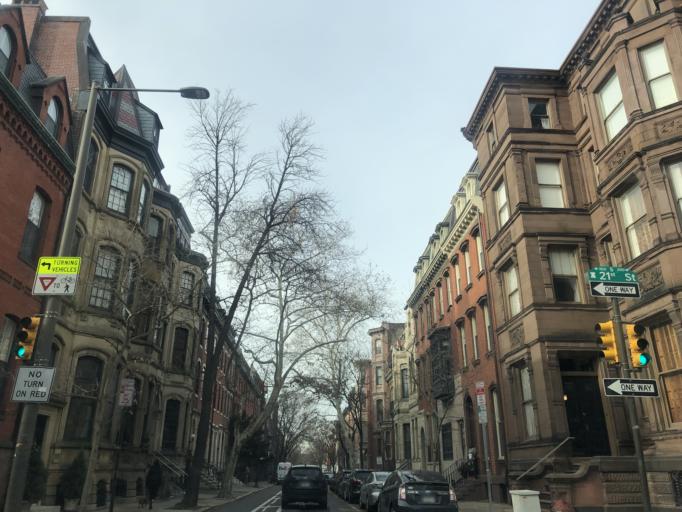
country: US
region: Pennsylvania
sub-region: Philadelphia County
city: Philadelphia
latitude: 39.9484
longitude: -75.1762
